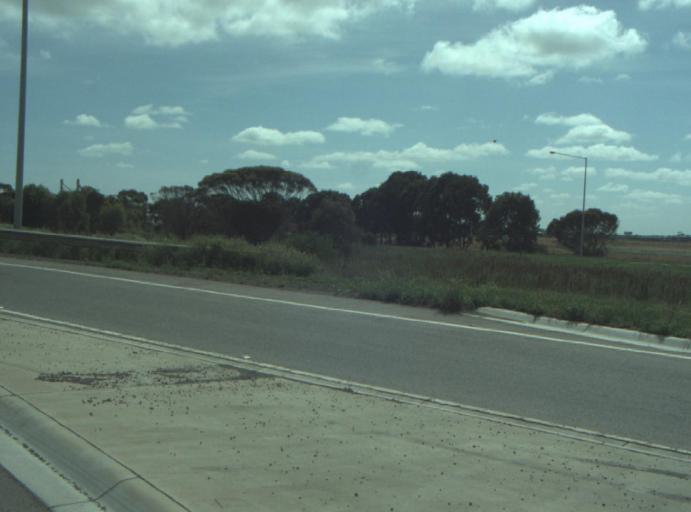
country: AU
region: Victoria
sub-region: Greater Geelong
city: Lara
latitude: -38.0324
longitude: 144.4316
